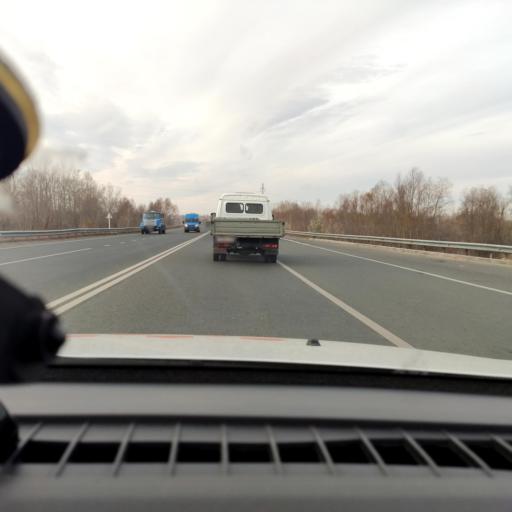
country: RU
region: Samara
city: Novokuybyshevsk
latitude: 53.1368
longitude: 49.9724
